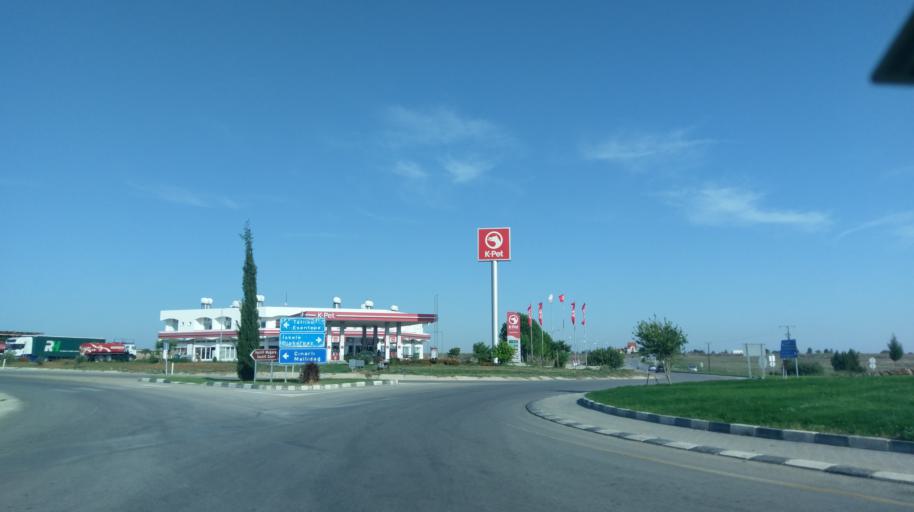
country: CY
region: Ammochostos
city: Lefkonoiko
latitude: 35.2619
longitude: 33.7469
